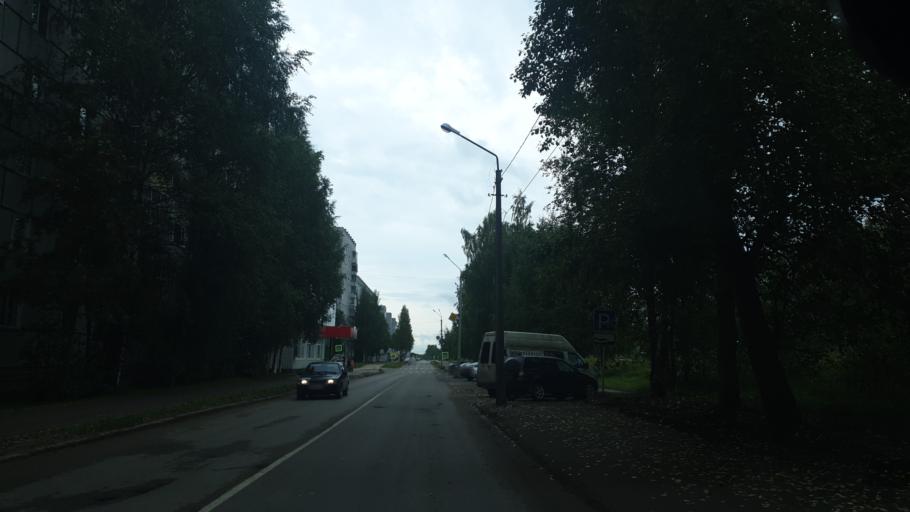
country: RU
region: Komi Republic
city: Ezhva
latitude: 61.7880
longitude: 50.7442
